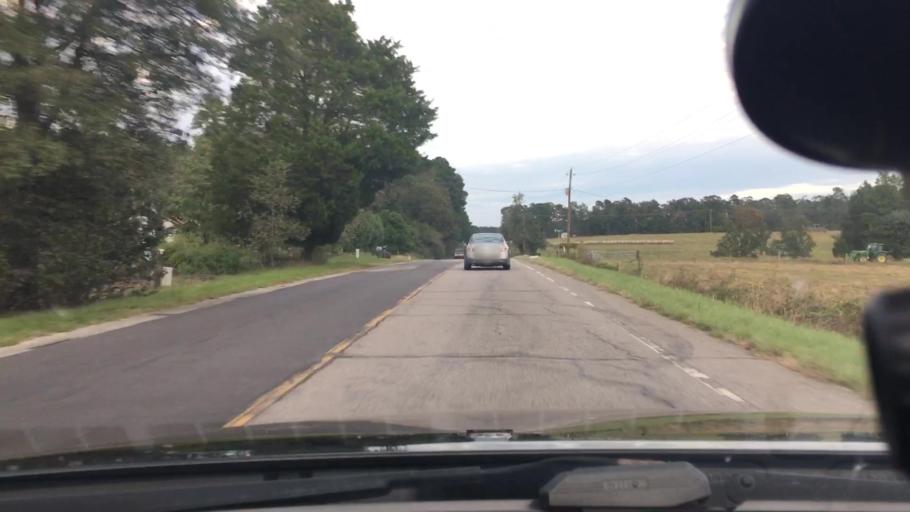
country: US
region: North Carolina
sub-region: Moore County
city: Carthage
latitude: 35.3592
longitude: -79.3301
